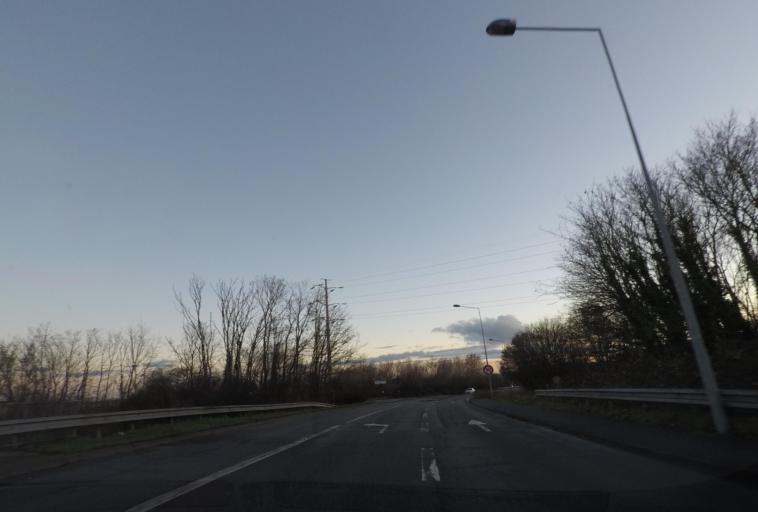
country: FR
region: Ile-de-France
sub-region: Departement de l'Essonne
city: Saint-Michel-sur-Orge
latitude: 48.6250
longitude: 2.3145
